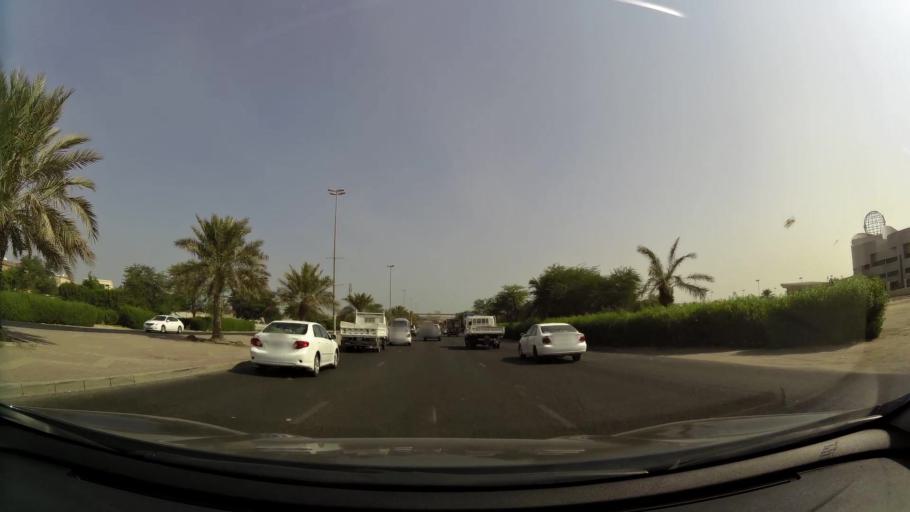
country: KW
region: Al Ahmadi
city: Al Fahahil
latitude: 29.0913
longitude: 48.1112
